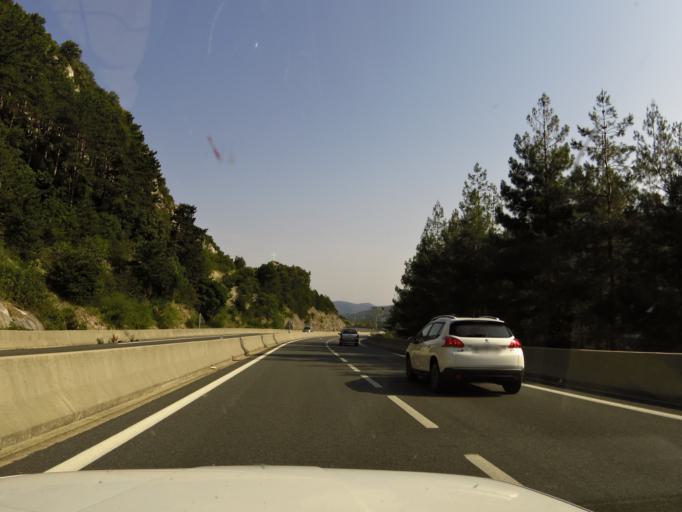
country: FR
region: Languedoc-Roussillon
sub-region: Departement de l'Herault
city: Lodeve
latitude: 43.8011
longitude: 3.3254
